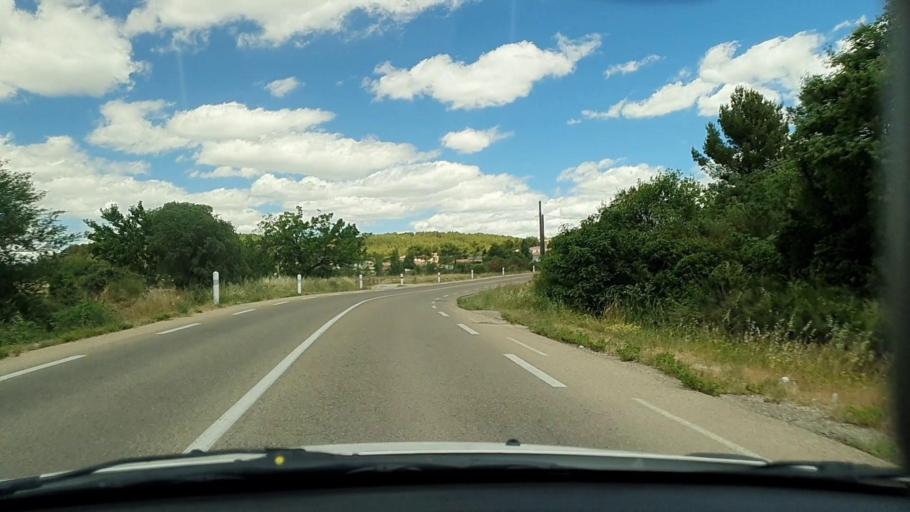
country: FR
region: Languedoc-Roussillon
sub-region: Departement du Gard
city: Marguerittes
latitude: 43.8705
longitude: 4.4085
